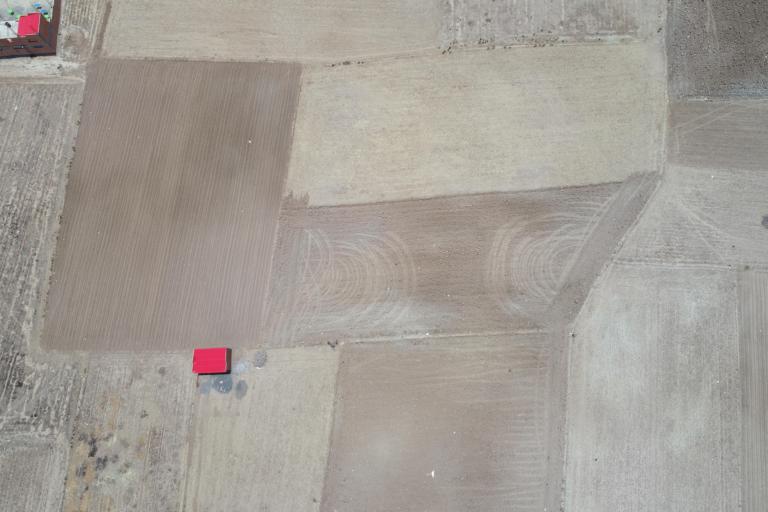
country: BO
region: La Paz
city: Achacachi
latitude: -16.0472
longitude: -68.6945
